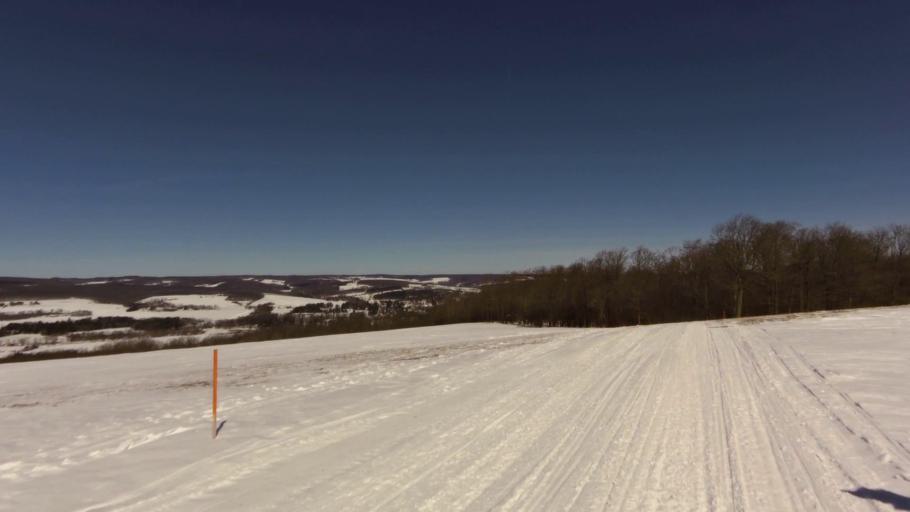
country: US
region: New York
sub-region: Allegany County
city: Houghton
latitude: 42.3666
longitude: -78.2554
